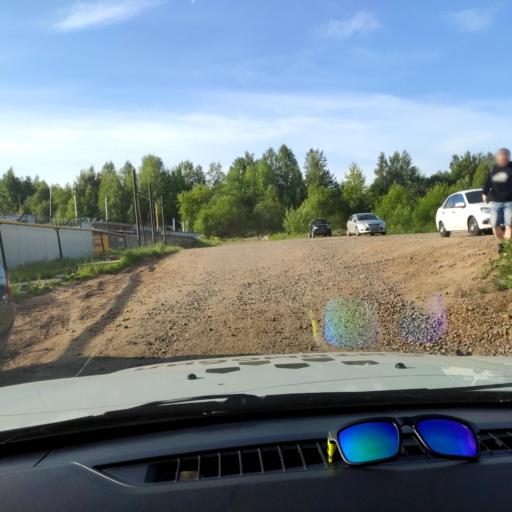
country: RU
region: Perm
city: Perm
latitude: 58.0708
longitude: 56.3758
